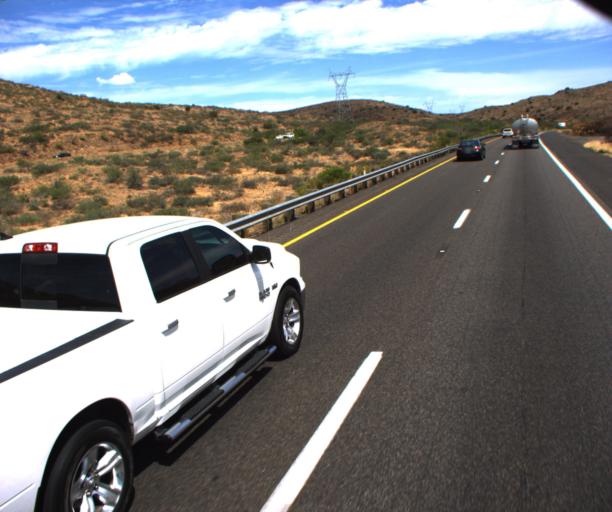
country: US
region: Arizona
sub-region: Yavapai County
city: Cordes Lakes
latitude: 34.2974
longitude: -112.1258
